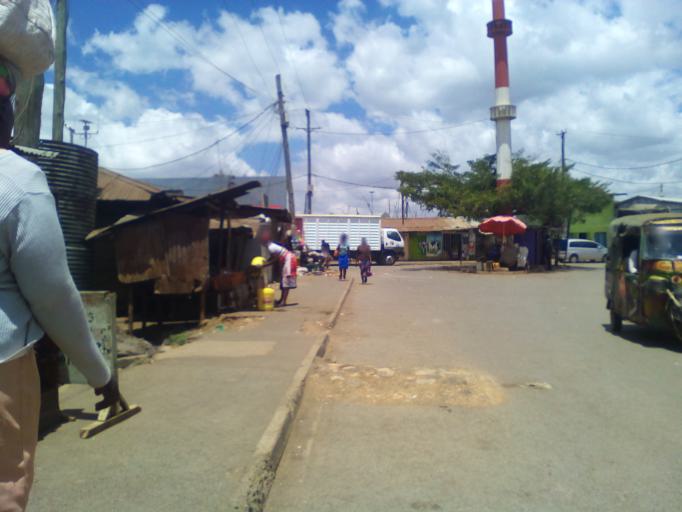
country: KE
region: Nairobi Area
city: Nairobi
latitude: -1.3089
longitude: 36.7856
